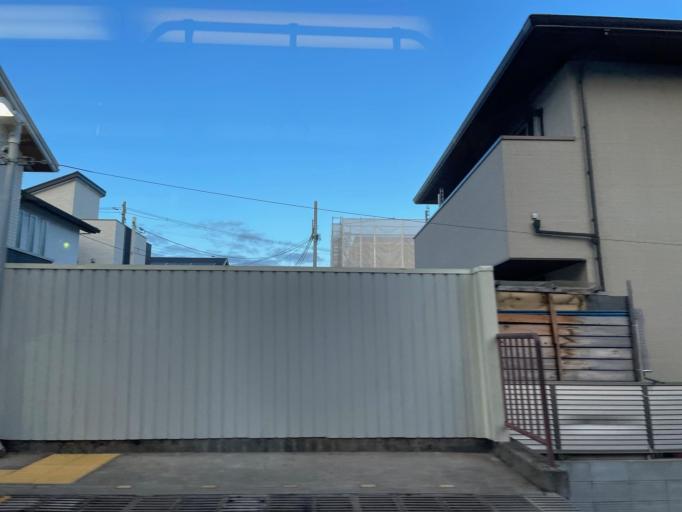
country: JP
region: Osaka
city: Sakai
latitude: 34.6228
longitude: 135.4984
